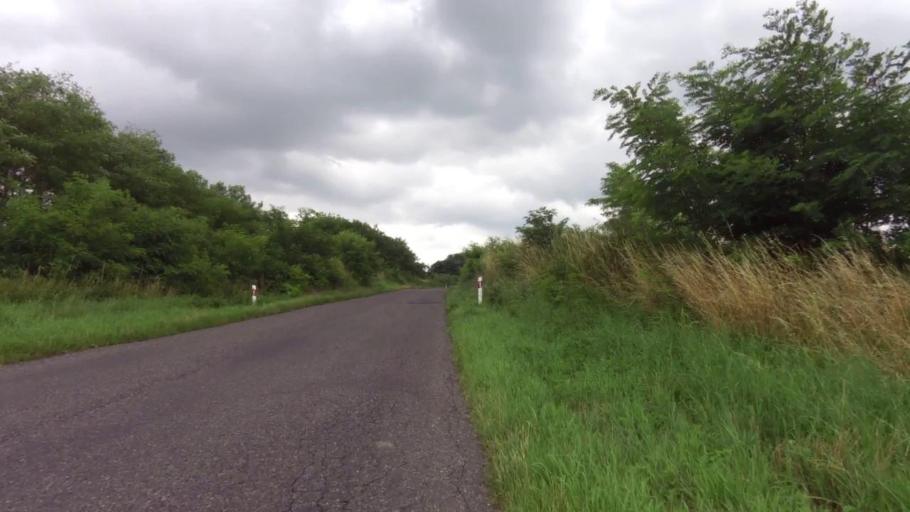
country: PL
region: West Pomeranian Voivodeship
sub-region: Powiat gryfinski
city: Cedynia
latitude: 52.8722
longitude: 14.2226
